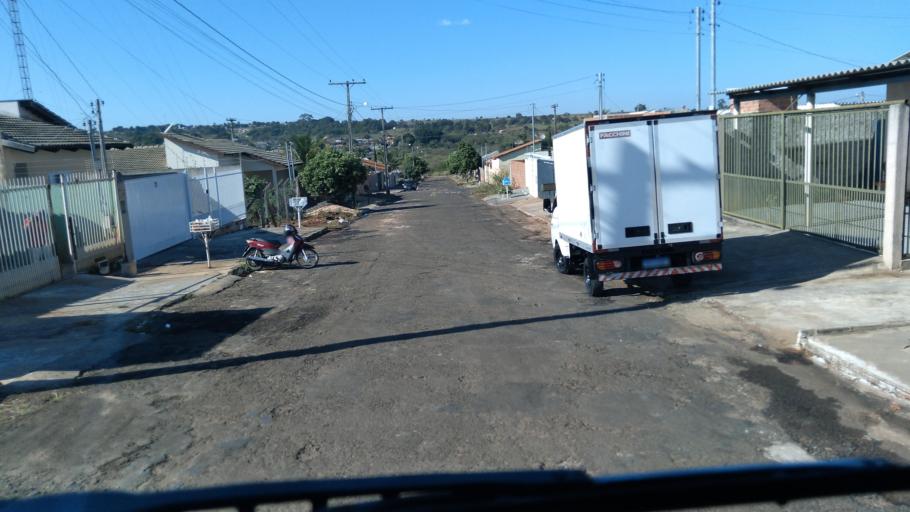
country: BR
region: Goias
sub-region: Mineiros
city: Mineiros
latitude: -17.5771
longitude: -52.5703
